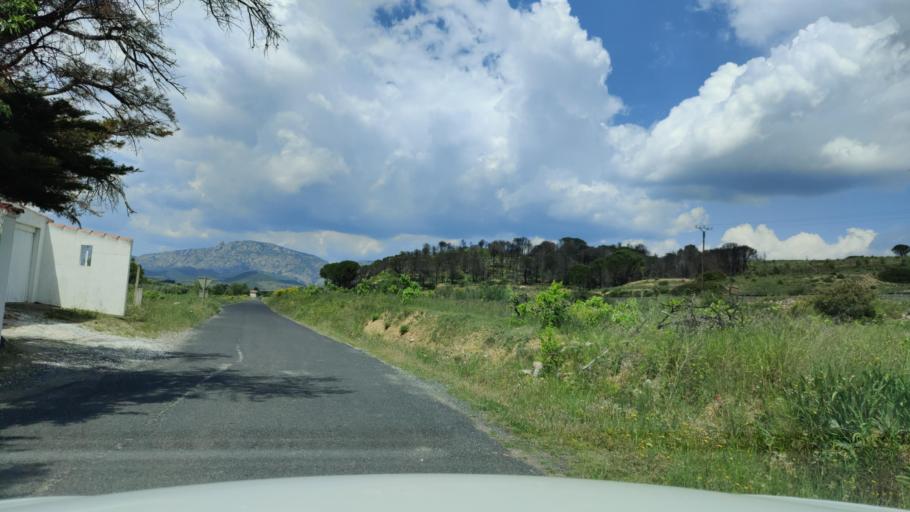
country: FR
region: Languedoc-Roussillon
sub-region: Departement des Pyrenees-Orientales
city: Estagel
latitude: 42.7895
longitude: 2.6806
